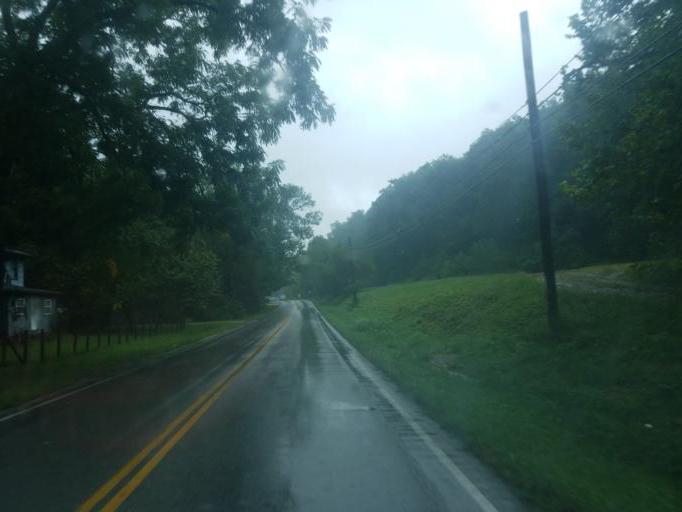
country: US
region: Kentucky
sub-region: Rowan County
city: Morehead
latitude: 38.2404
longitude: -83.3495
